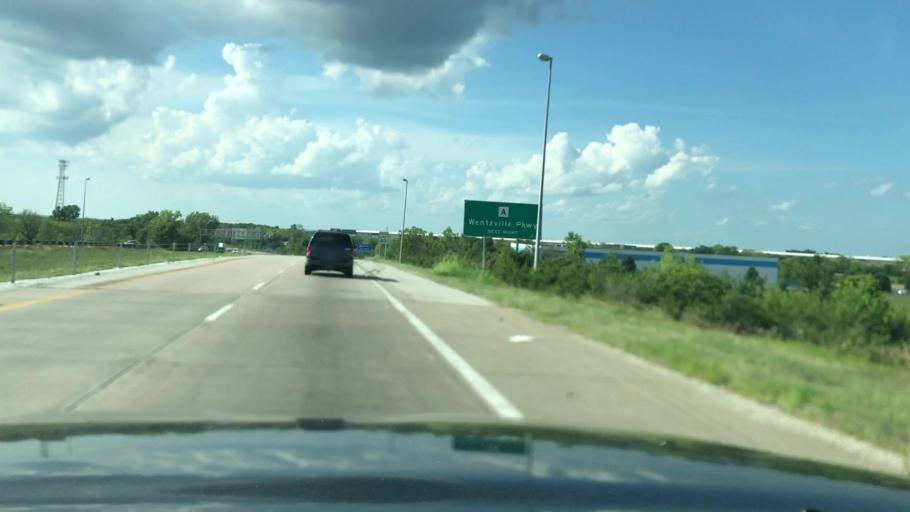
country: US
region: Missouri
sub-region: Saint Charles County
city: Wentzville
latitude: 38.8135
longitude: -90.8419
